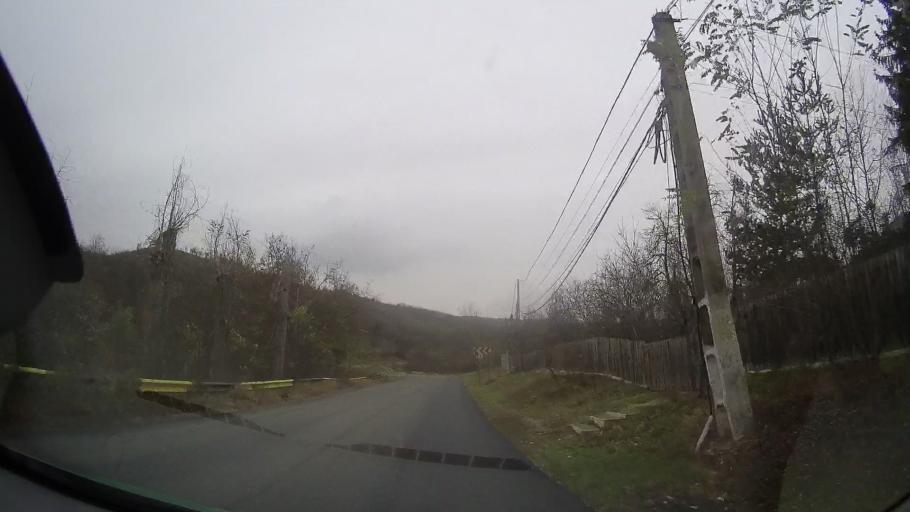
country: RO
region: Prahova
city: Ceptura de Sus
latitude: 45.0464
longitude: 26.3030
